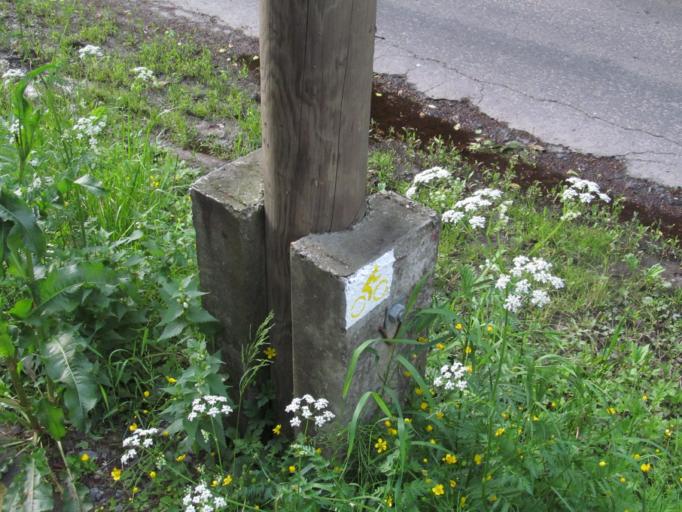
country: HU
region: Borsod-Abauj-Zemplen
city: Gonc
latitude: 48.5267
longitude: 21.4350
